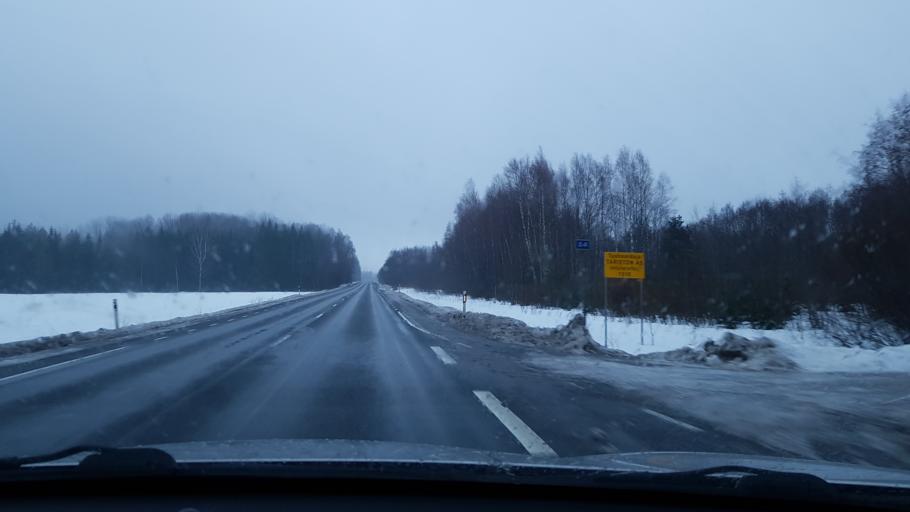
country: EE
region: Jaervamaa
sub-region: Tueri vald
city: Sarevere
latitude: 58.8050
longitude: 25.2156
